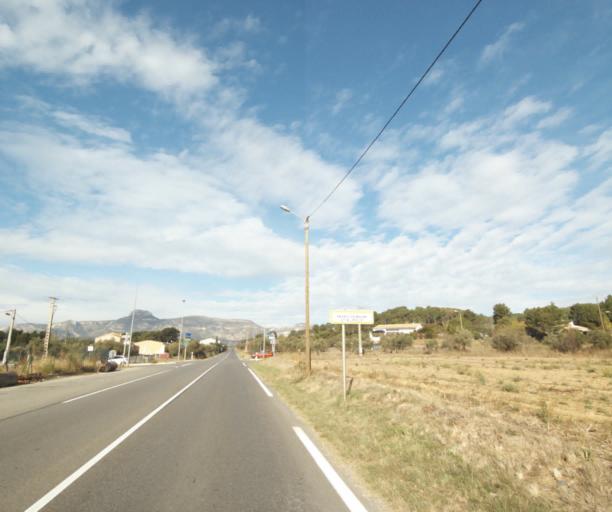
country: FR
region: Provence-Alpes-Cote d'Azur
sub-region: Departement des Bouches-du-Rhone
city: Gemenos
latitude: 43.3084
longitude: 5.6086
